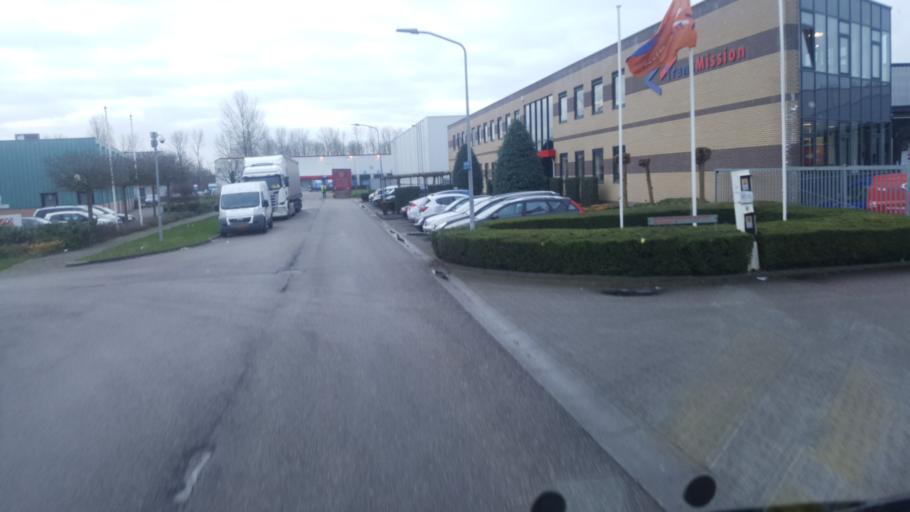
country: NL
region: Flevoland
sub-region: Gemeente Almere
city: Almere Stad
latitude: 52.3644
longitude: 5.1735
